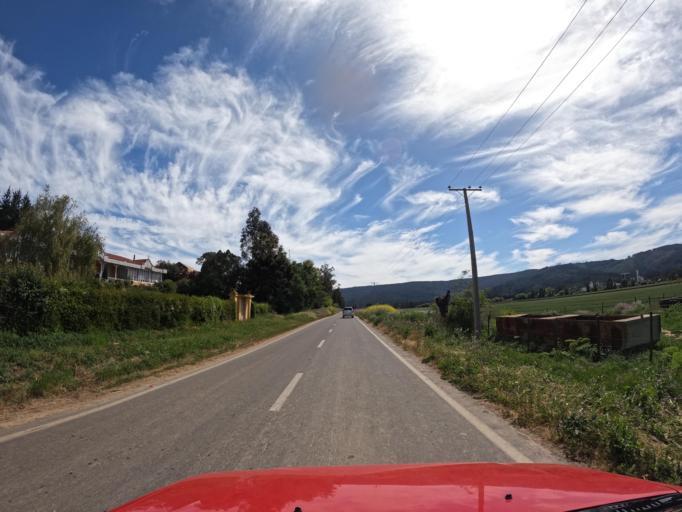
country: CL
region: Maule
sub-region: Provincia de Talca
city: Constitucion
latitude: -34.9940
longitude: -72.0123
